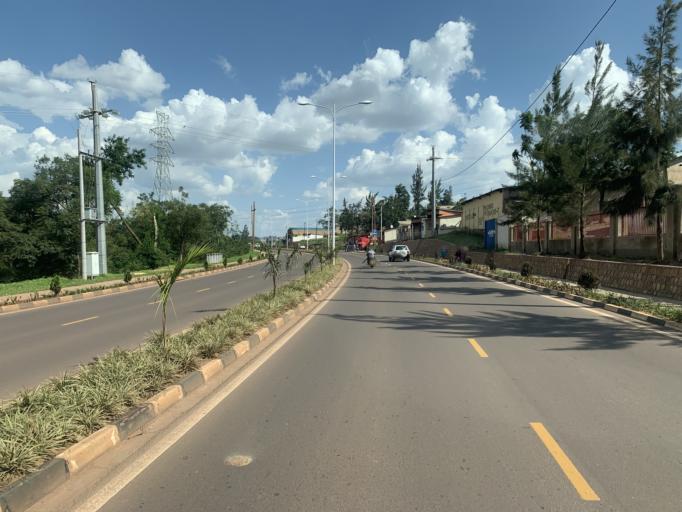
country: RW
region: Kigali
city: Kigali
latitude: -1.9632
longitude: 30.0779
